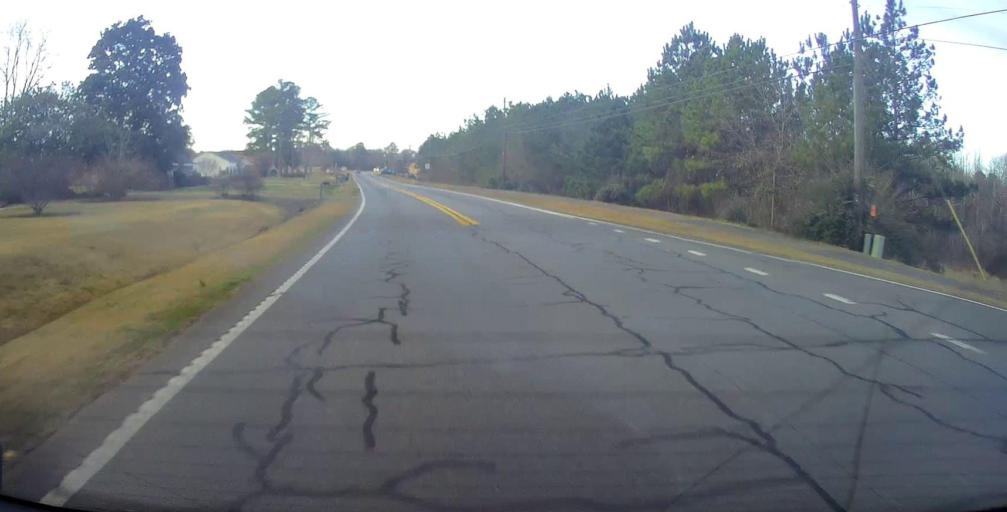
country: US
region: Georgia
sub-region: Talbot County
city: Sardis
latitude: 32.7784
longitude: -84.5581
